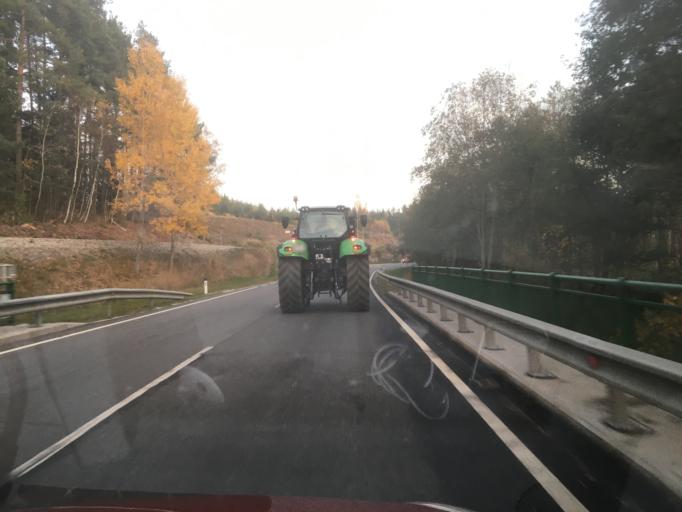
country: AT
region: Lower Austria
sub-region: Politischer Bezirk Zwettl
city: Langschlag
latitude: 48.5748
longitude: 14.8985
